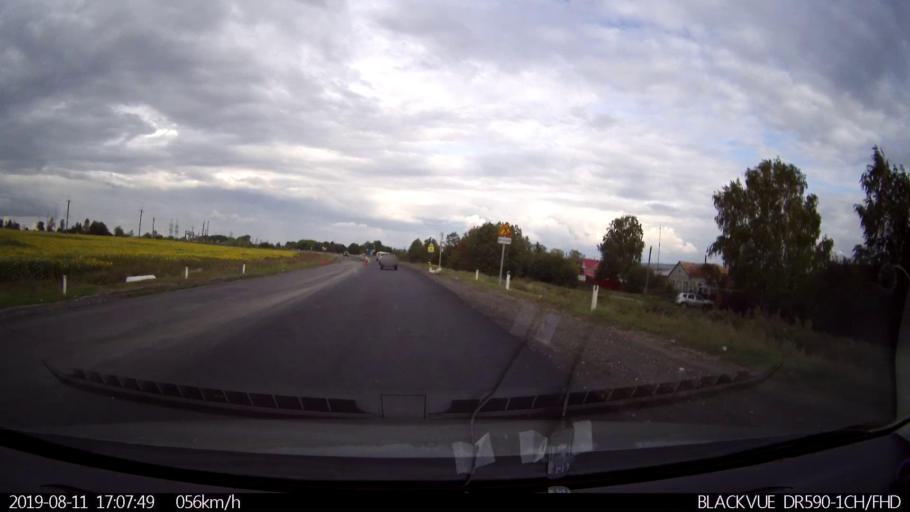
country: RU
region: Ulyanovsk
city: Mayna
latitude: 54.2918
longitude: 47.8305
